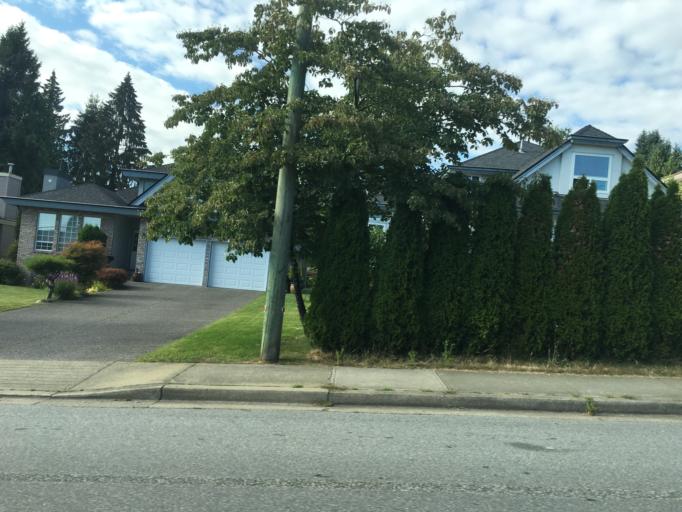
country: CA
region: British Columbia
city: New Westminster
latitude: 49.2454
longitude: -122.8843
